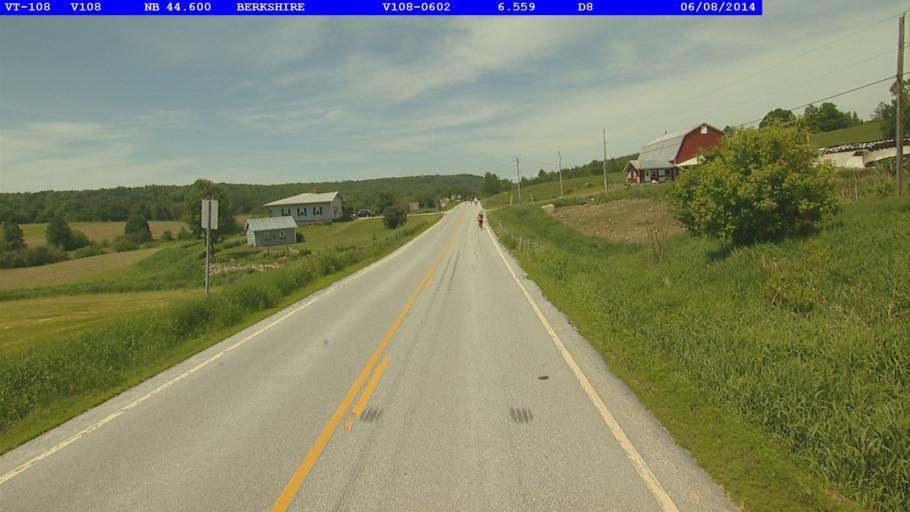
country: US
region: Vermont
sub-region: Franklin County
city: Enosburg Falls
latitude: 45.0115
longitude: -72.8249
